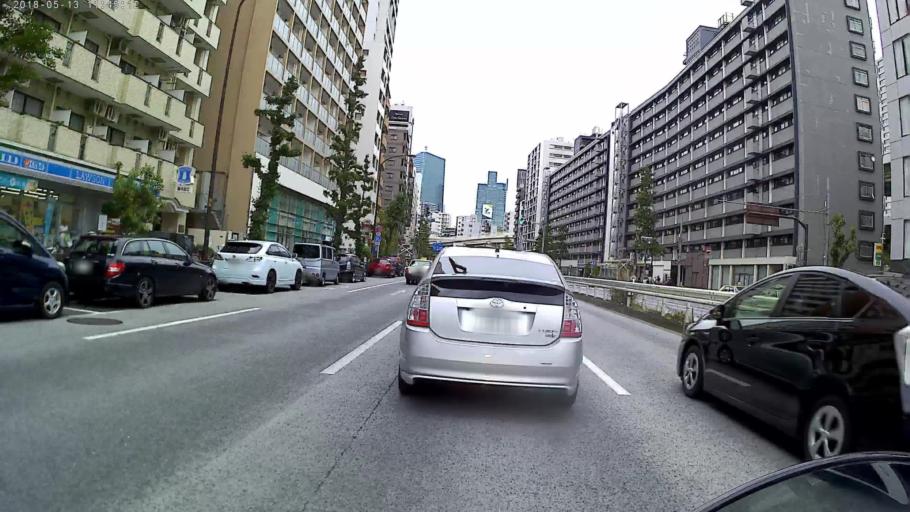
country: JP
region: Tokyo
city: Tokyo
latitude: 35.6535
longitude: 139.7367
